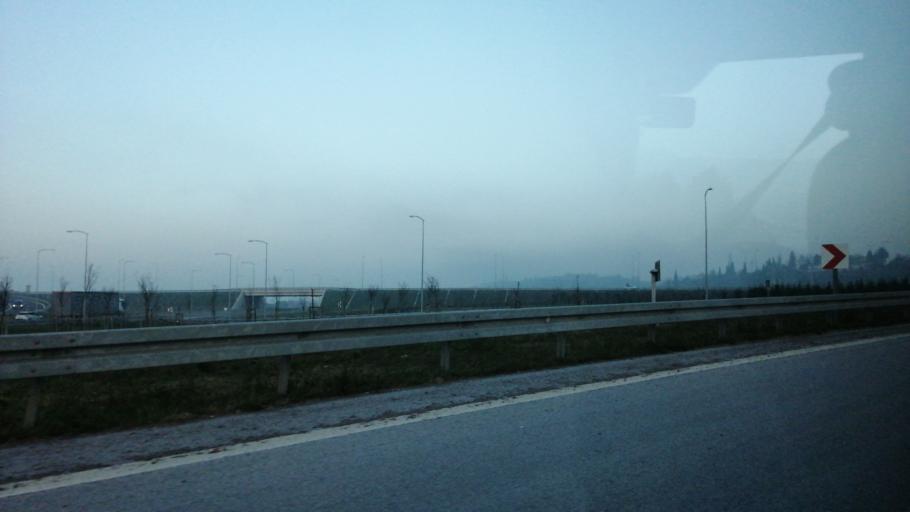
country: TR
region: Yalova
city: Altinova
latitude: 40.6897
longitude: 29.4679
